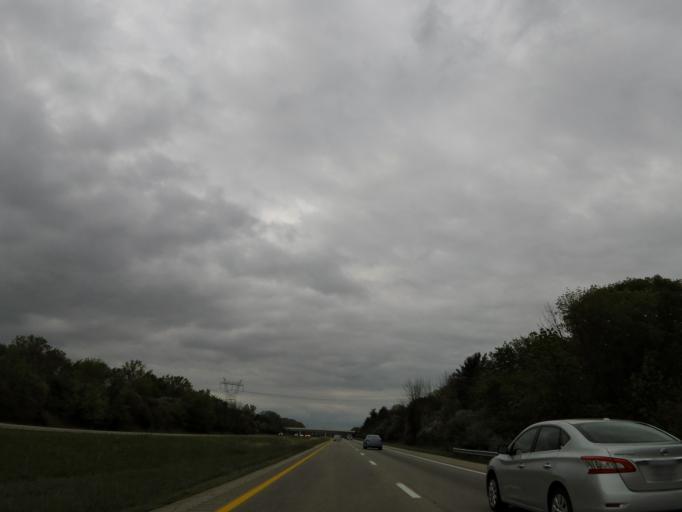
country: US
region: Ohio
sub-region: Madison County
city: Mount Sterling
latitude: 39.8099
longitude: -83.1936
